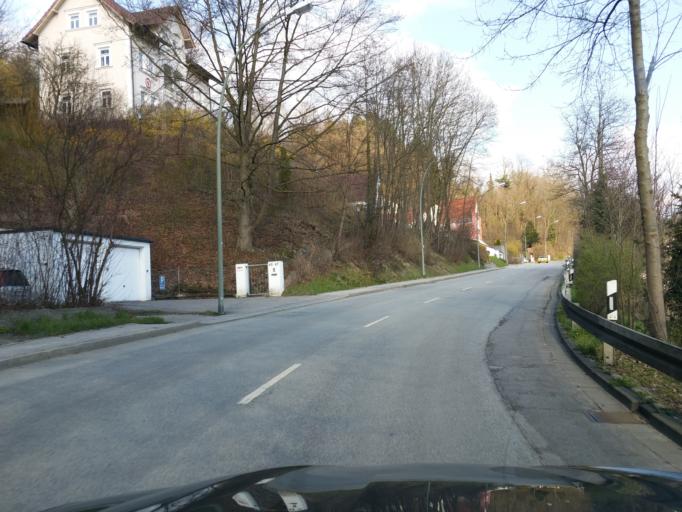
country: DE
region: Bavaria
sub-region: Lower Bavaria
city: Landshut
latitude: 48.5258
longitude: 12.1466
